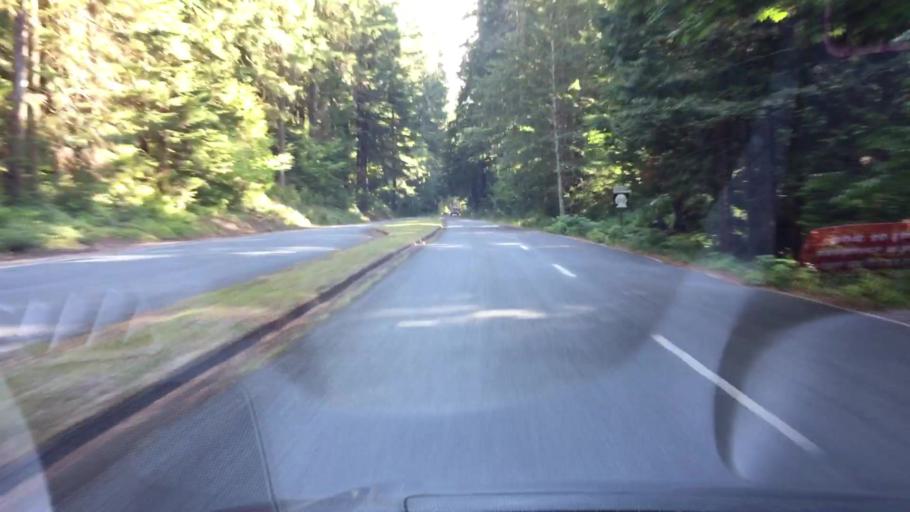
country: US
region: Washington
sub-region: Pierce County
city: Buckley
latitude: 46.7321
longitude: -121.5690
